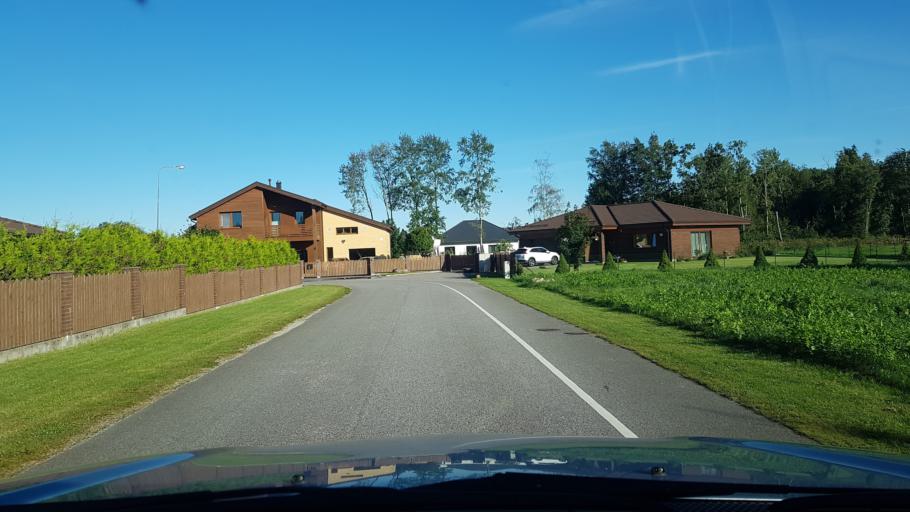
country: EE
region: Harju
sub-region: Rae vald
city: Jueri
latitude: 59.3877
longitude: 24.8563
